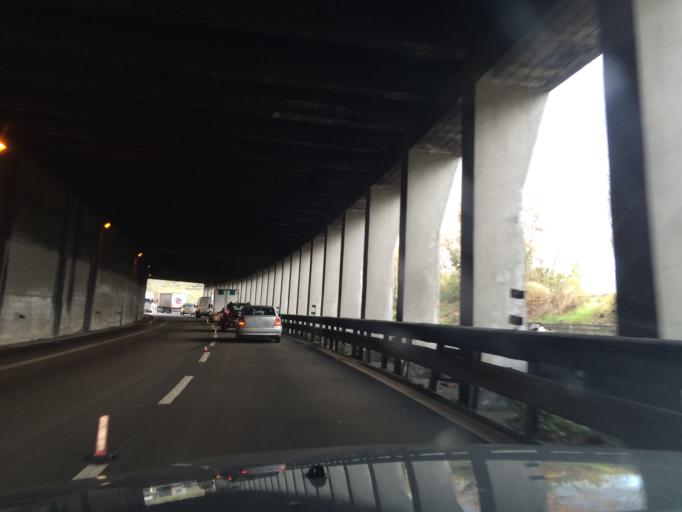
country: IT
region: Umbria
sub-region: Provincia di Terni
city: Narni Scalo
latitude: 42.5415
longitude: 12.4994
